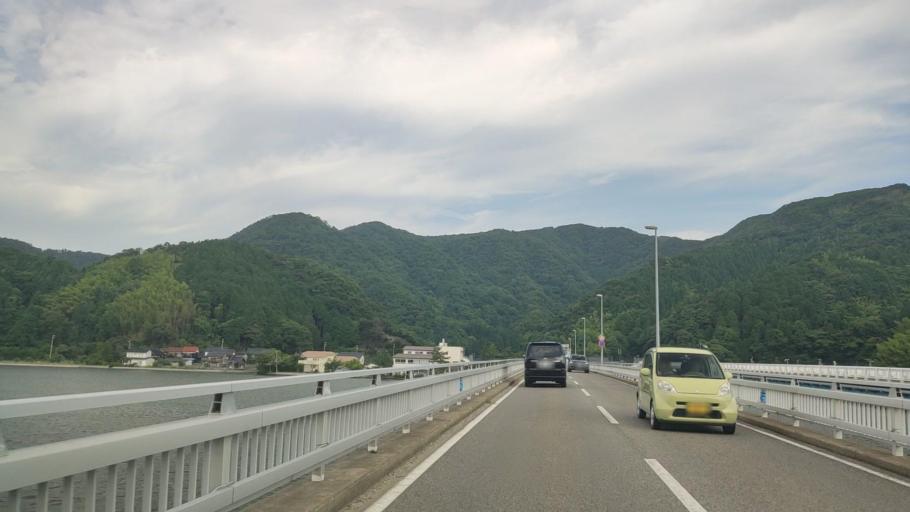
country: JP
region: Hyogo
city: Toyooka
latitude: 35.6411
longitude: 134.8273
